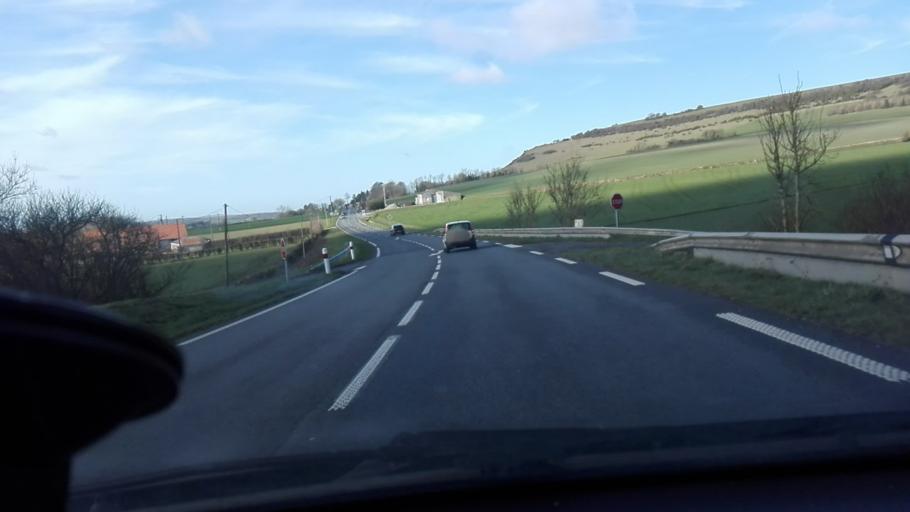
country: FR
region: Nord-Pas-de-Calais
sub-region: Departement du Pas-de-Calais
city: Licques
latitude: 50.7315
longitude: 1.8924
